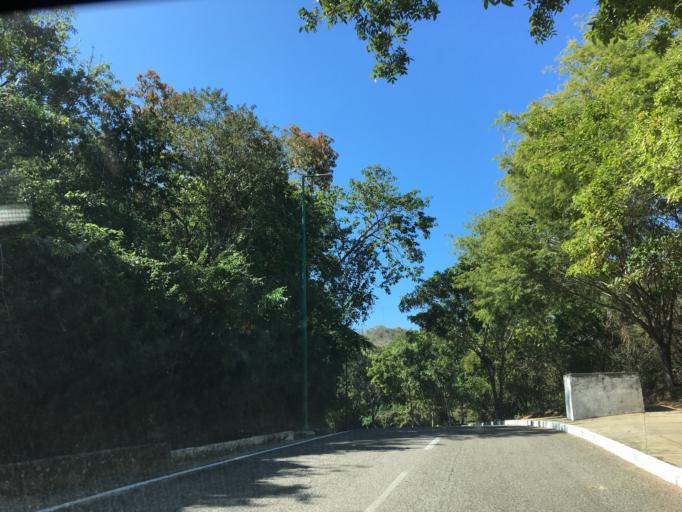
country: MX
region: Oaxaca
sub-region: Santa Maria Huatulco
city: Crucecita
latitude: 15.7810
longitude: -96.0763
